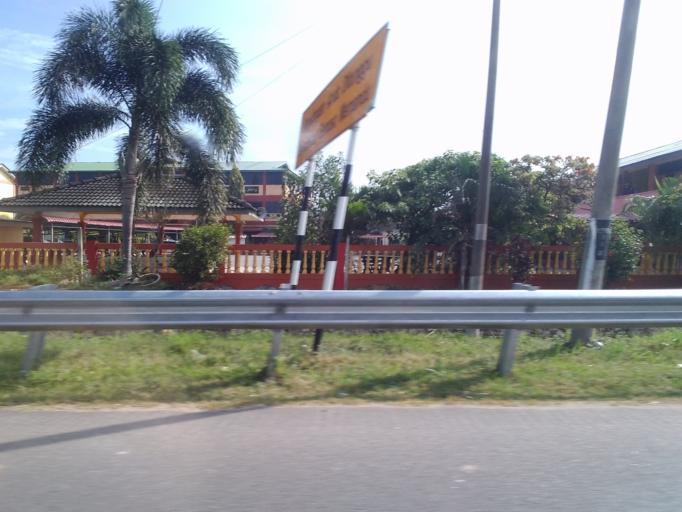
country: MY
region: Kedah
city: Gurun
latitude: 5.9519
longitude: 100.4083
